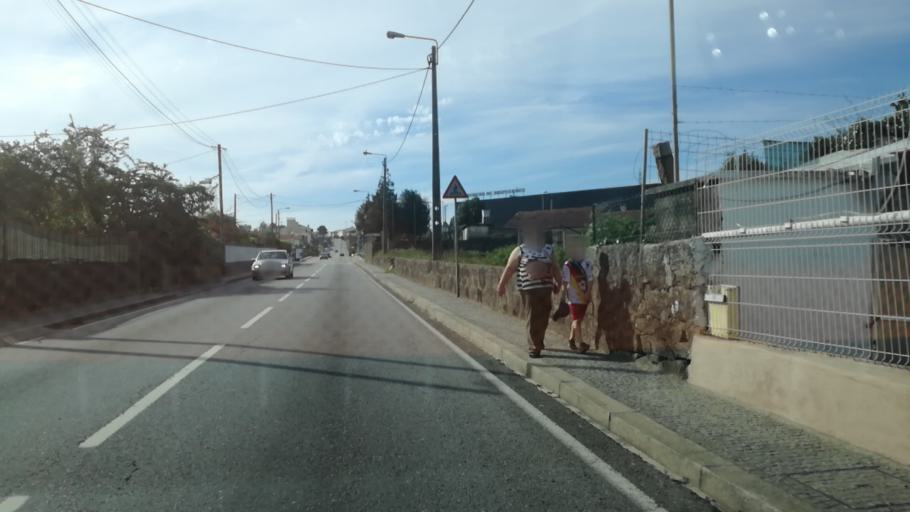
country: PT
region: Porto
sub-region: Valongo
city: Ermesinde
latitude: 41.2282
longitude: -8.5686
